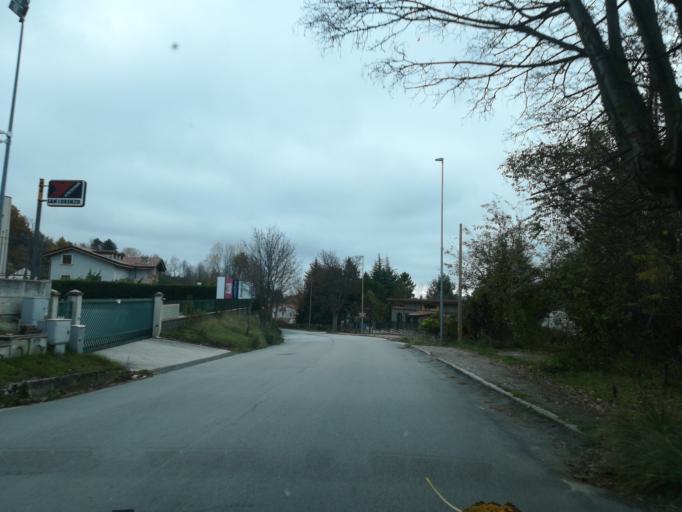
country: IT
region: Molise
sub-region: Provincia di Isernia
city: Agnone
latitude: 41.8161
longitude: 14.3729
